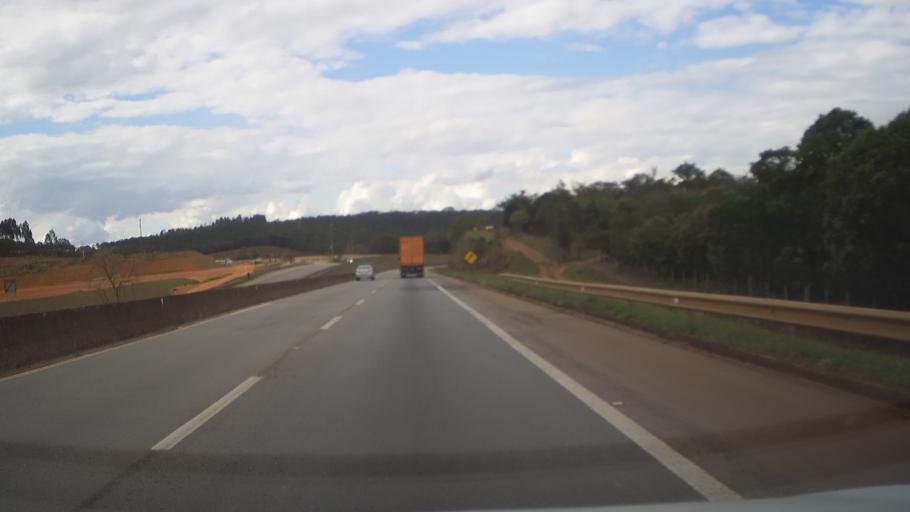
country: BR
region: Minas Gerais
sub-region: Itauna
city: Itauna
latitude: -20.2890
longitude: -44.4358
